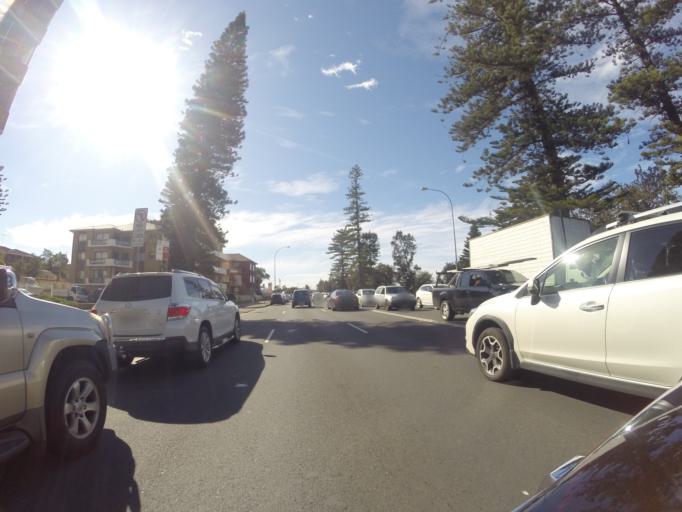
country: AU
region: New South Wales
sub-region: Rockdale
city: Brighton-Le-Sands
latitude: -33.9593
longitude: 151.1571
